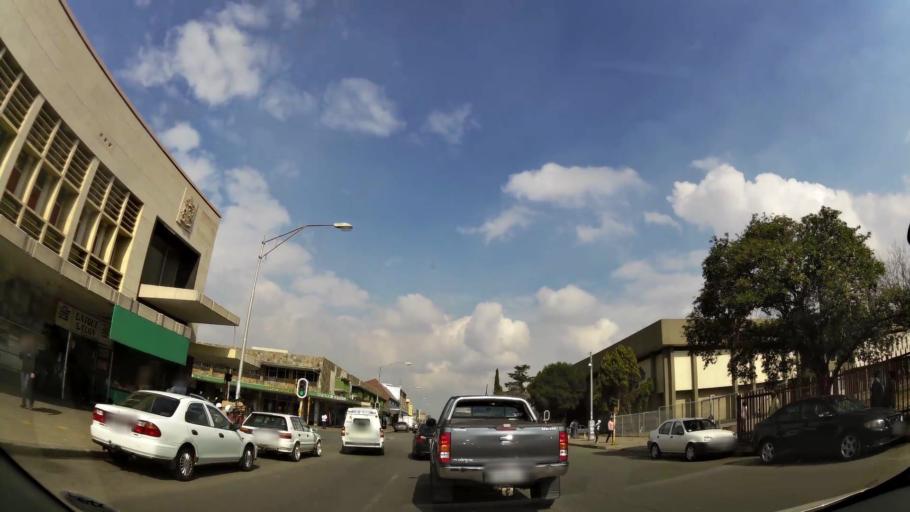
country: ZA
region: Gauteng
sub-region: Sedibeng District Municipality
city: Vereeniging
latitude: -26.6743
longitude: 27.9295
